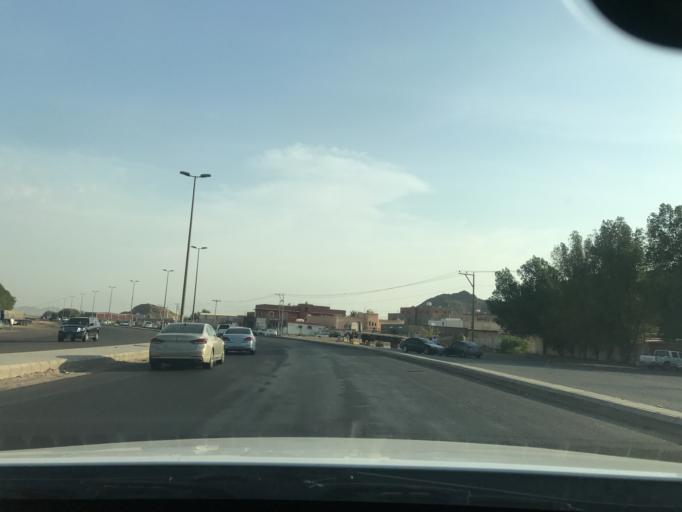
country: SA
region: Makkah
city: Jeddah
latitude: 21.4046
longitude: 39.4272
